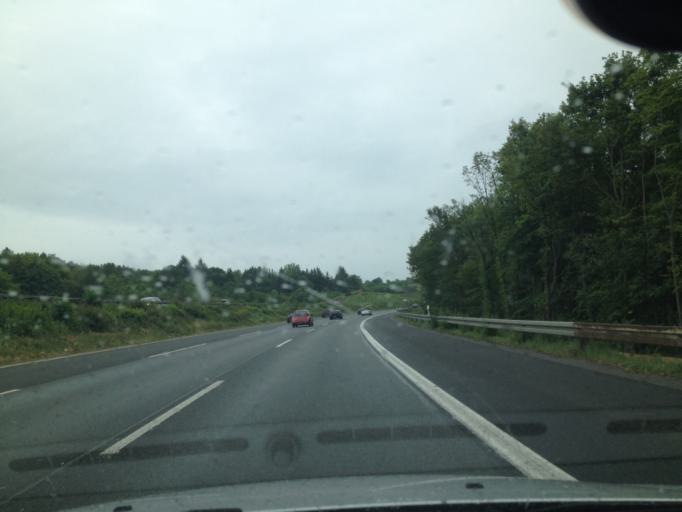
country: DE
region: Bavaria
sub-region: Regierungsbezirk Unterfranken
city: Randersacker
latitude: 49.7411
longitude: 9.9709
